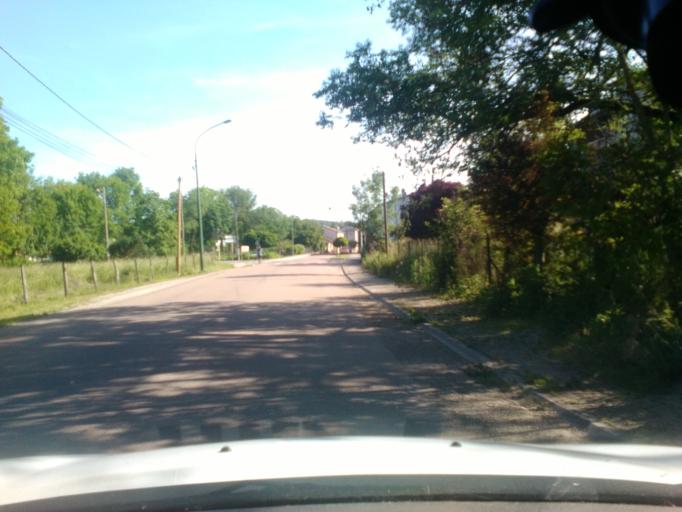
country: FR
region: Lorraine
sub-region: Departement des Vosges
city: Mirecourt
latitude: 48.2261
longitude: 6.2202
